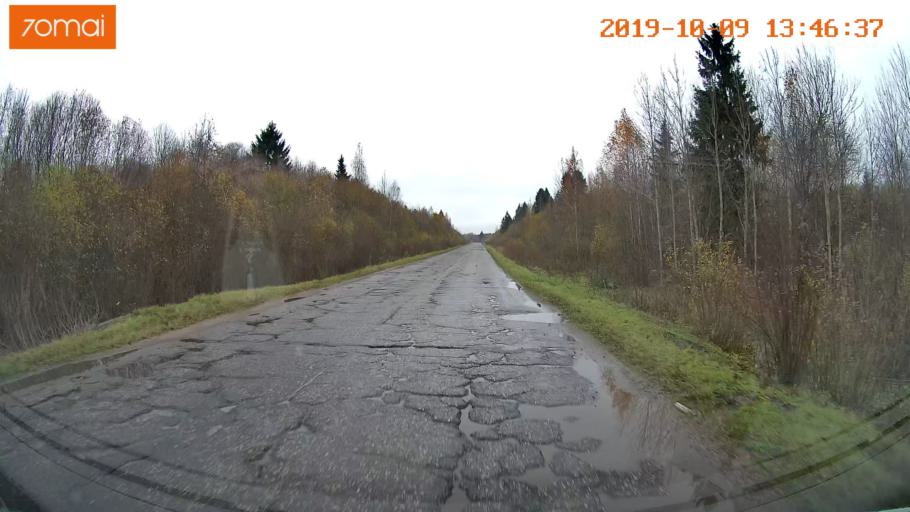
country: RU
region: Kostroma
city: Buy
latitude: 58.3849
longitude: 41.2190
